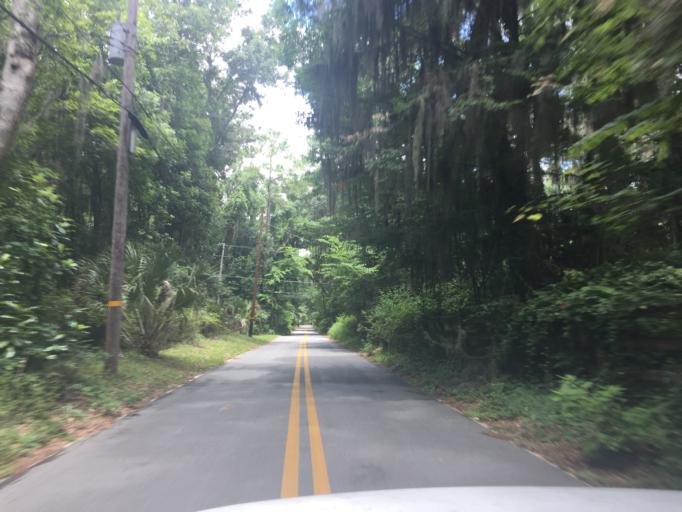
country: US
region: Georgia
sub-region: Chatham County
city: Montgomery
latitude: 31.9403
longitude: -81.1160
